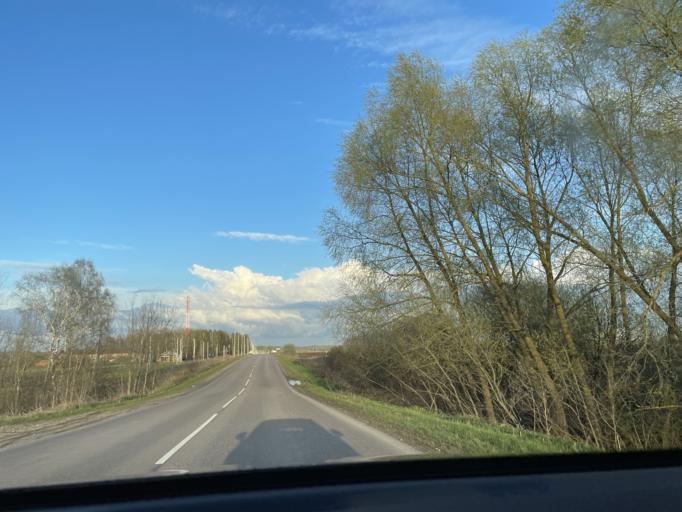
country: RU
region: Tula
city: Novogurovskiy
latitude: 54.5271
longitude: 37.4039
